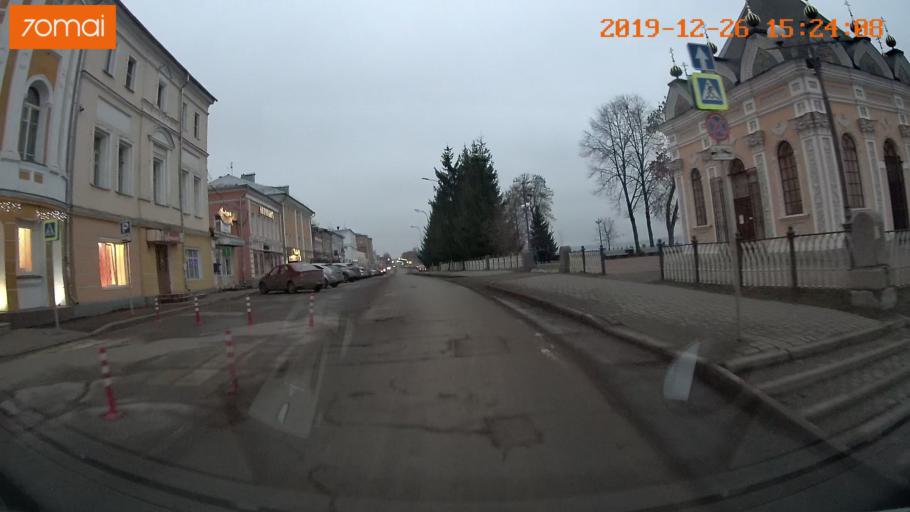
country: RU
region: Jaroslavl
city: Rybinsk
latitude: 58.0501
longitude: 38.8526
